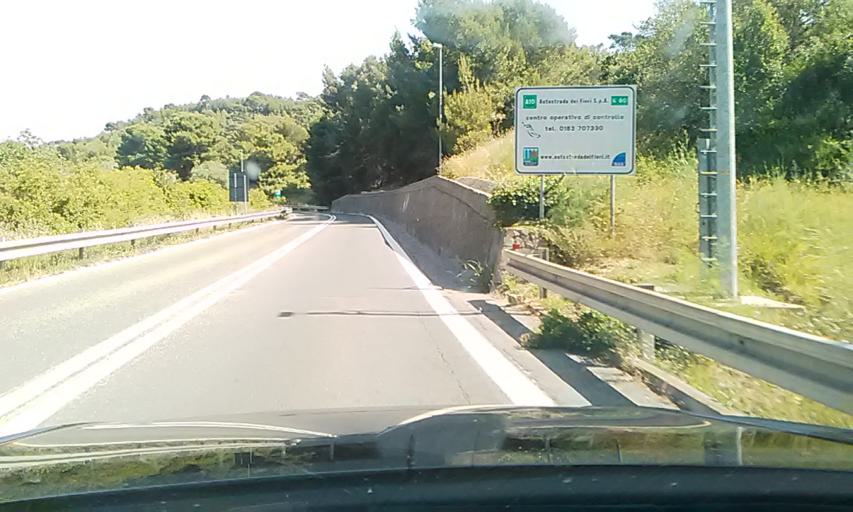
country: IT
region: Liguria
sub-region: Provincia di Savona
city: Andora
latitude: 43.9697
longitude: 8.1427
